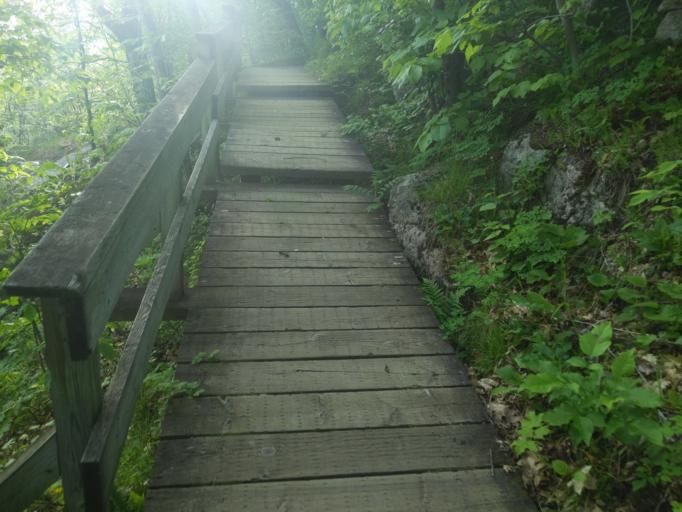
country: CA
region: Quebec
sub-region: Outaouais
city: Wakefield
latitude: 45.5102
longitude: -75.9147
